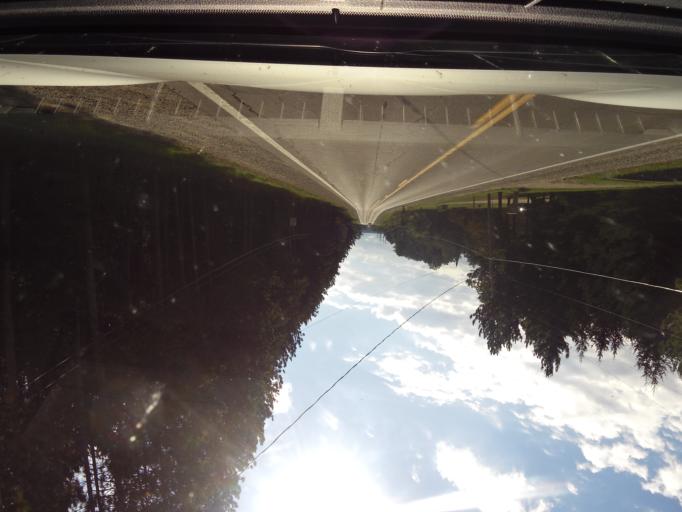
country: US
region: Michigan
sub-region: Roscommon County
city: Roscommon
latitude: 44.5072
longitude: -84.5825
